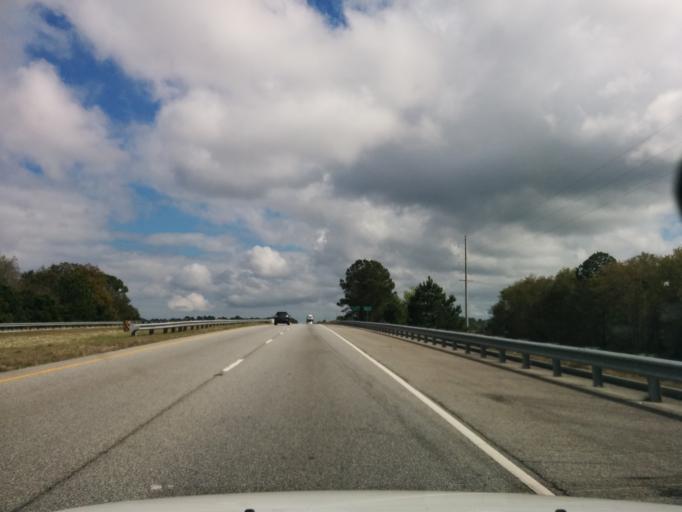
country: US
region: Georgia
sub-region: Glynn County
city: Brunswick
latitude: 31.1282
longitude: -81.5544
